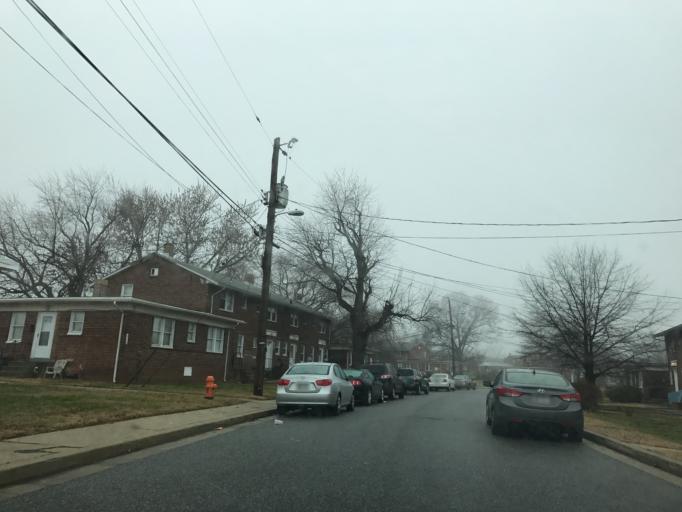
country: US
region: Maryland
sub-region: Baltimore County
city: Dundalk
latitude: 39.2363
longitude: -76.5049
